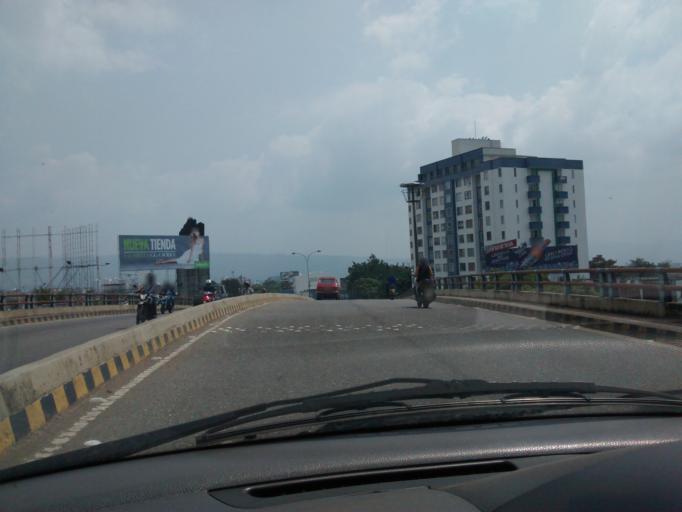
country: CO
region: Santander
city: Bucaramanga
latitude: 7.1060
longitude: -73.1137
